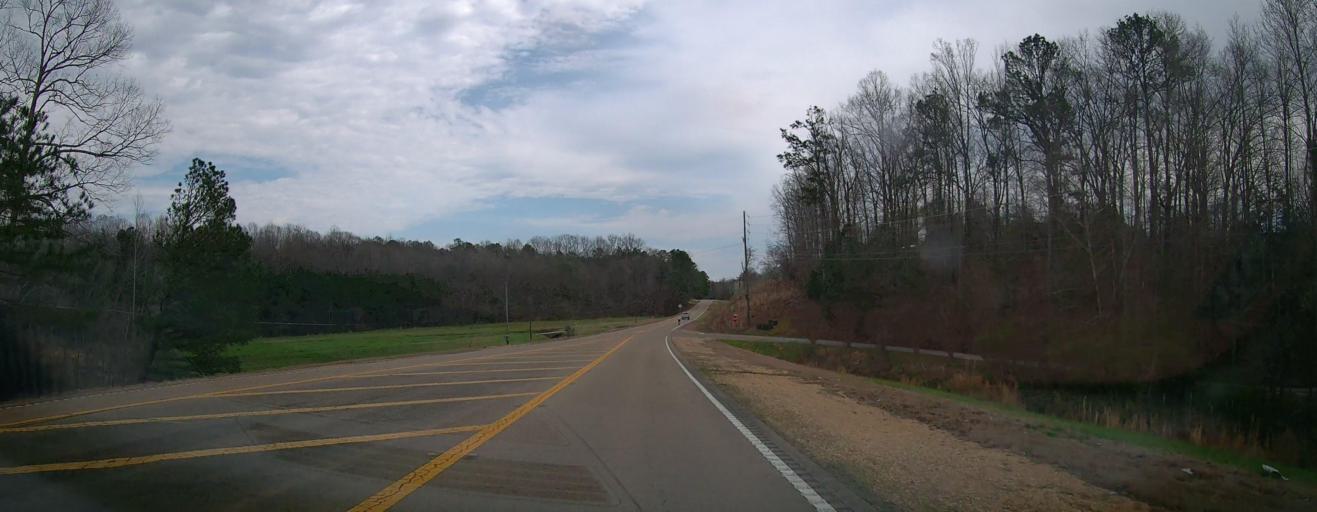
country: US
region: Mississippi
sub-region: Itawamba County
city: Fulton
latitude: 34.2634
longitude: -88.3268
